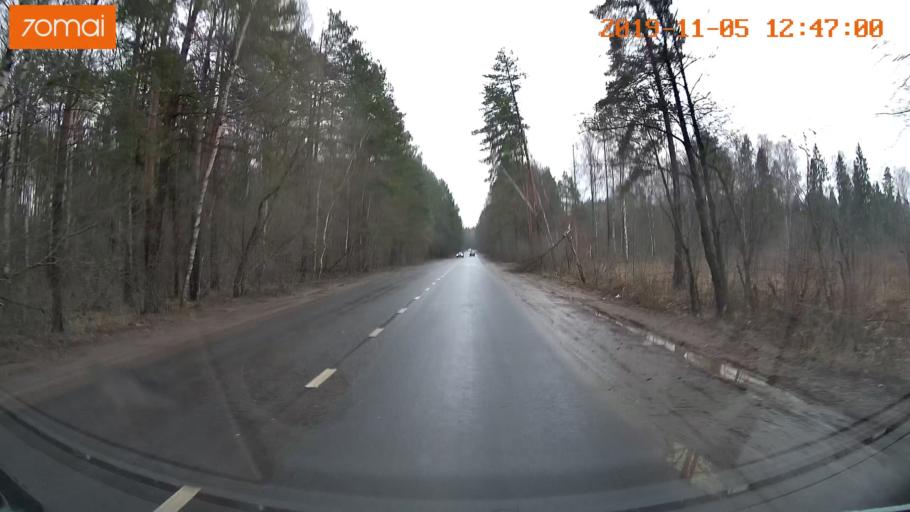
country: RU
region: Ivanovo
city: Kokhma
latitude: 56.9709
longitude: 41.0827
